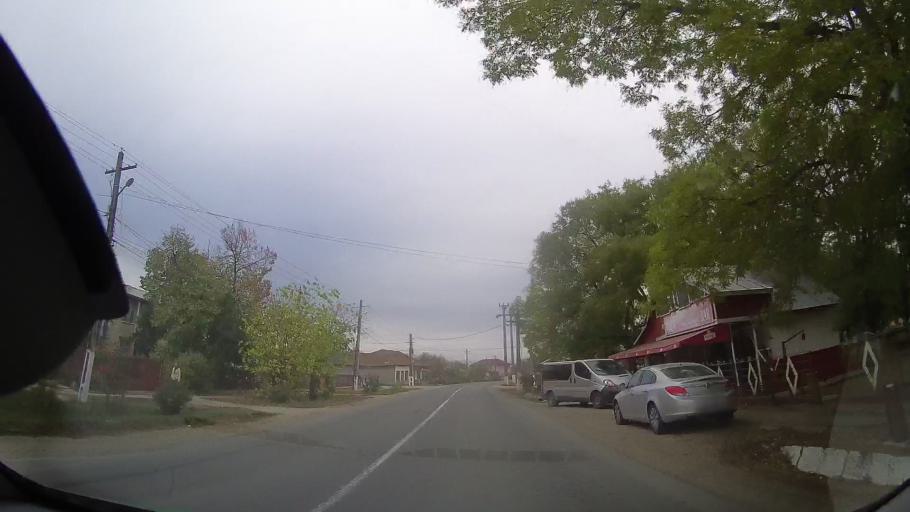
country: RO
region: Ialomita
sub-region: Comuna Grivita
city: Grivita
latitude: 44.7356
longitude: 27.2902
